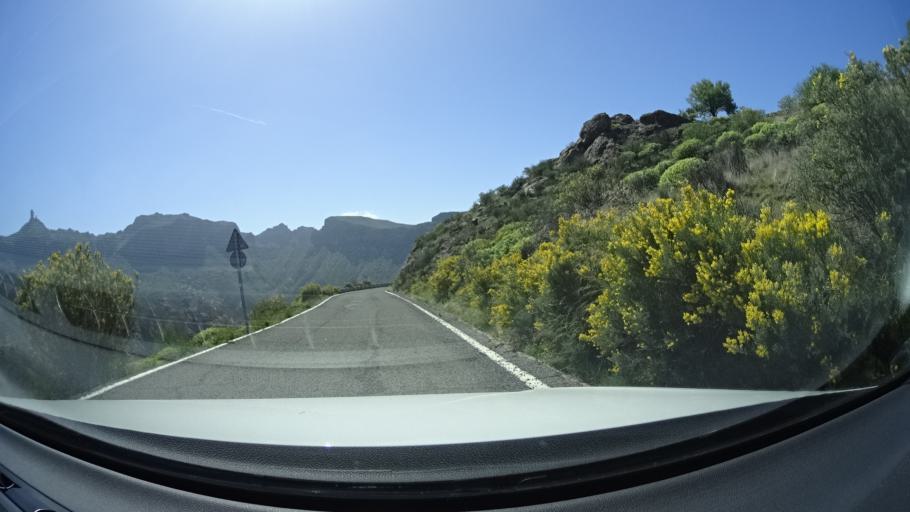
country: ES
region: Canary Islands
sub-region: Provincia de Las Palmas
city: Tejeda
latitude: 27.9898
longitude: -15.6374
